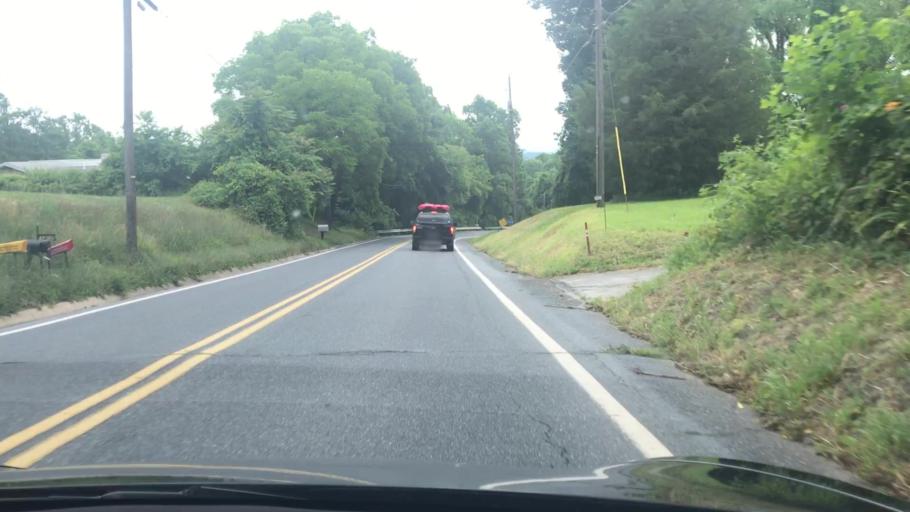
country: US
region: Pennsylvania
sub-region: York County
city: Valley Green
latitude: 40.1103
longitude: -76.7699
